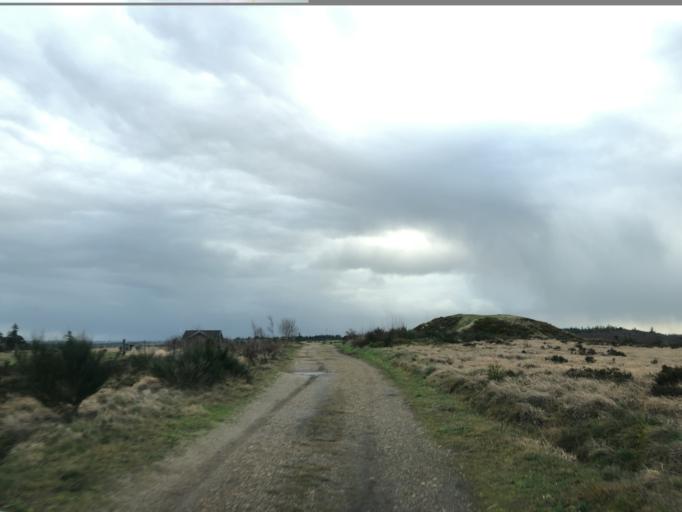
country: DK
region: Central Jutland
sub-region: Ringkobing-Skjern Kommune
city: Videbaek
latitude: 56.1835
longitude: 8.6632
